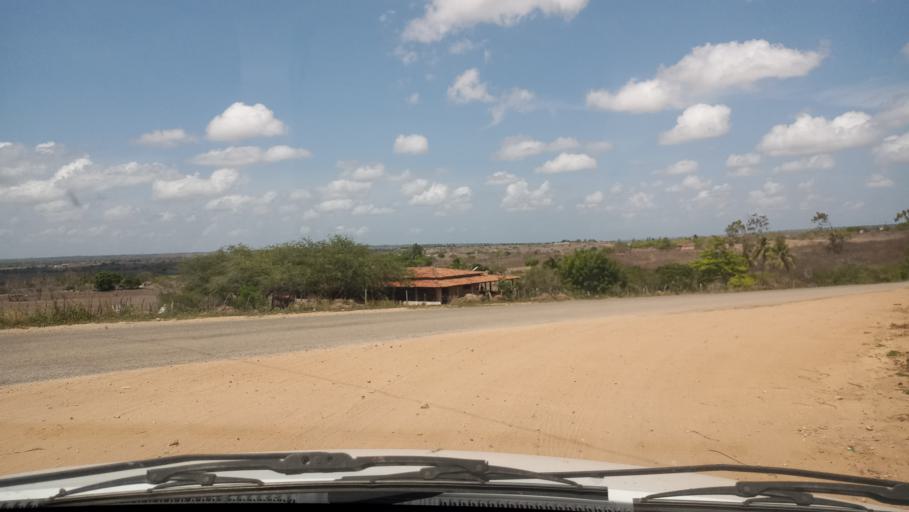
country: BR
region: Rio Grande do Norte
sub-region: Goianinha
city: Goianinha
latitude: -6.3401
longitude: -35.3262
